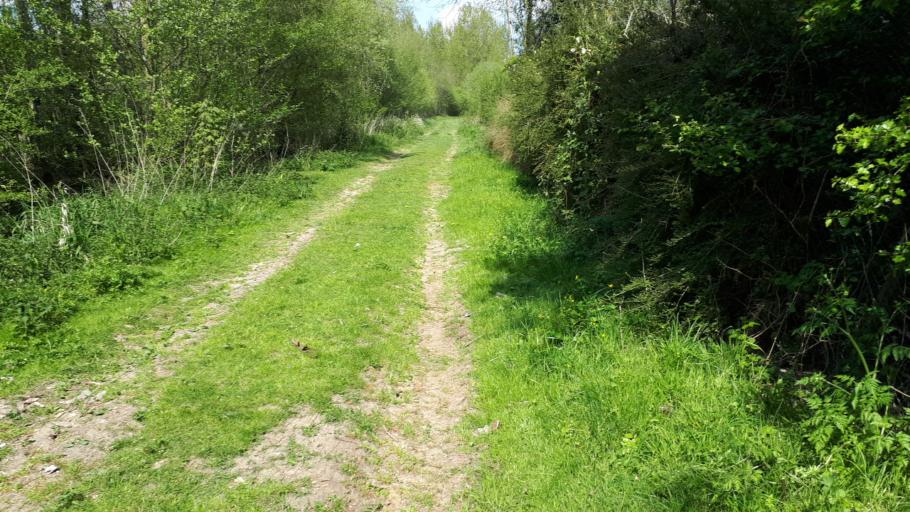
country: FR
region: Centre
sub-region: Departement du Loir-et-Cher
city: Villiers-sur-Loir
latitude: 47.8252
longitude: 0.9756
